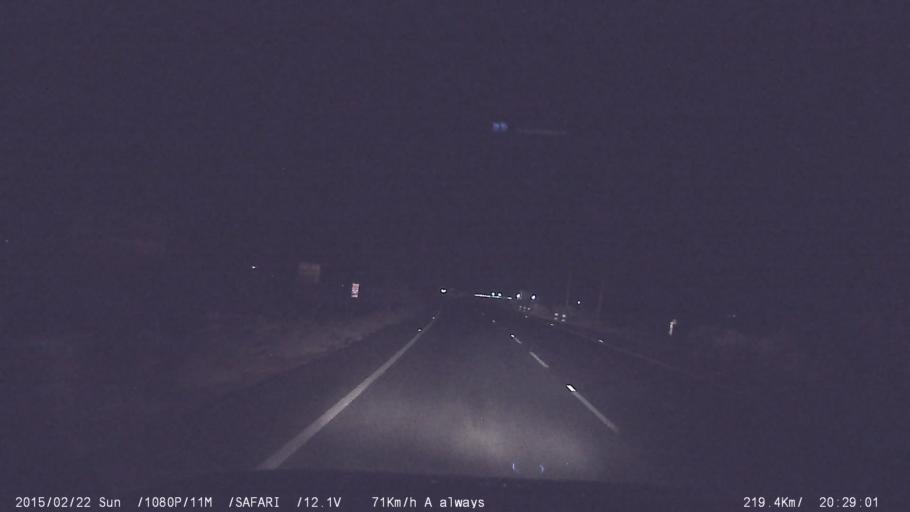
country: IN
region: Tamil Nadu
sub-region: Dindigul
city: Dindigul
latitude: 10.3308
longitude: 77.9267
